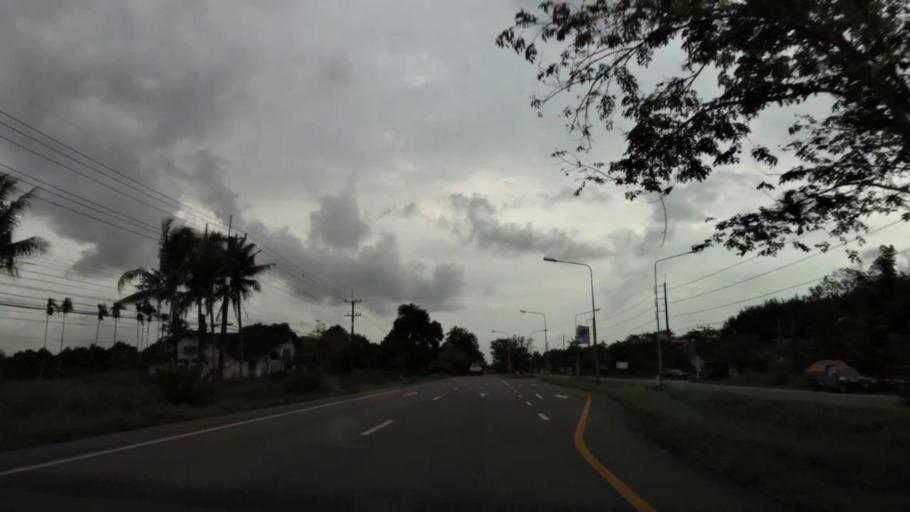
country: TH
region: Chanthaburi
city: Tha Mai
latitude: 12.7098
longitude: 101.9821
